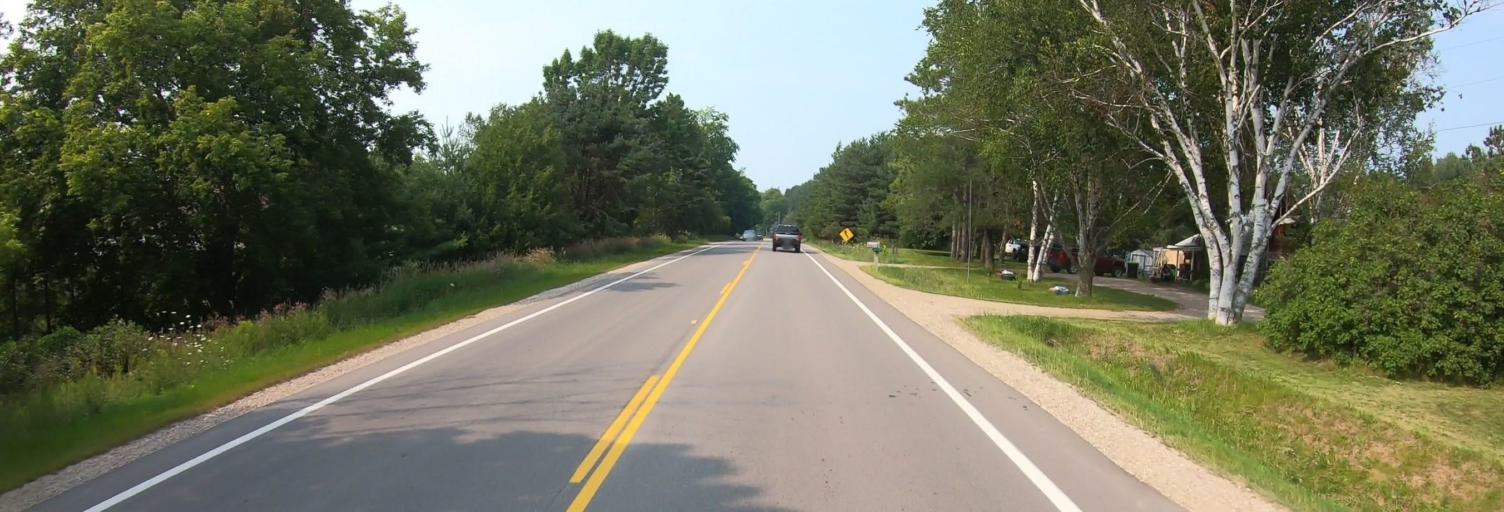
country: US
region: Michigan
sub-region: Charlevoix County
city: Charlevoix
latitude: 45.2525
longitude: -85.2612
